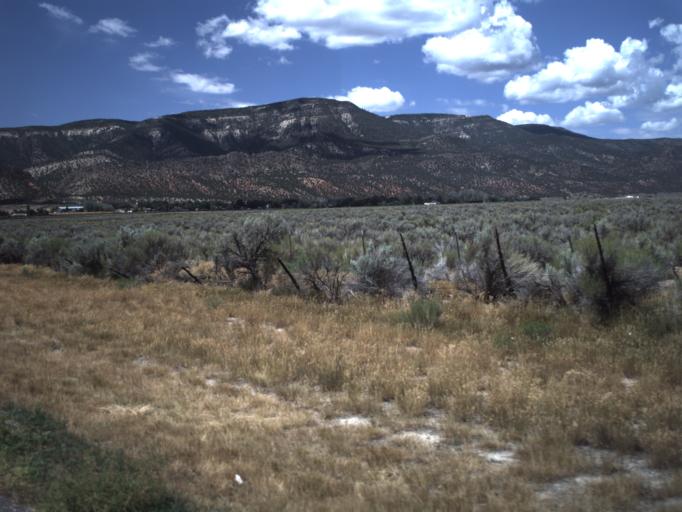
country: US
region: Utah
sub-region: Sanpete County
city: Moroni
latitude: 39.4755
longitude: -111.6171
